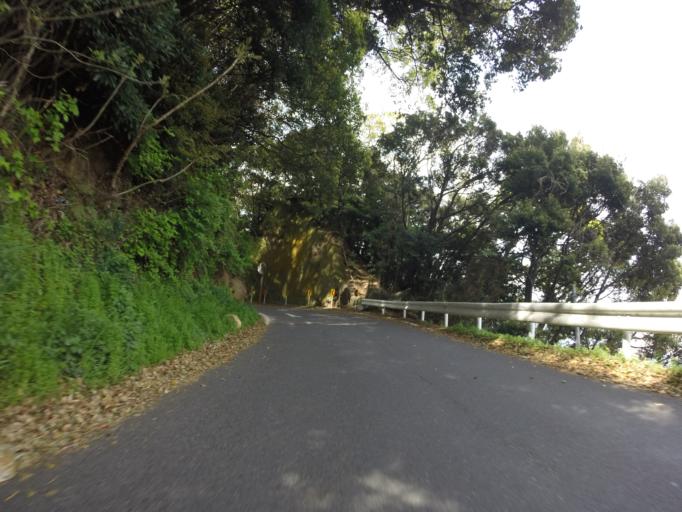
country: JP
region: Shizuoka
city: Heda
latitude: 35.0188
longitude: 138.8360
